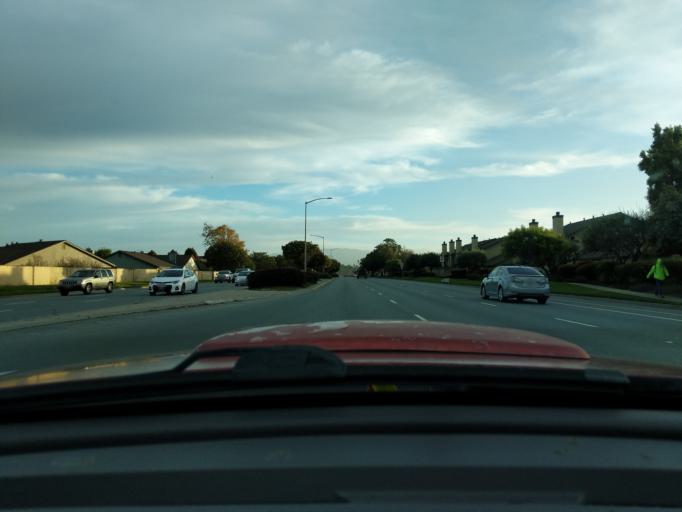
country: US
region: California
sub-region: Monterey County
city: Boronda
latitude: 36.7112
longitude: -121.6543
